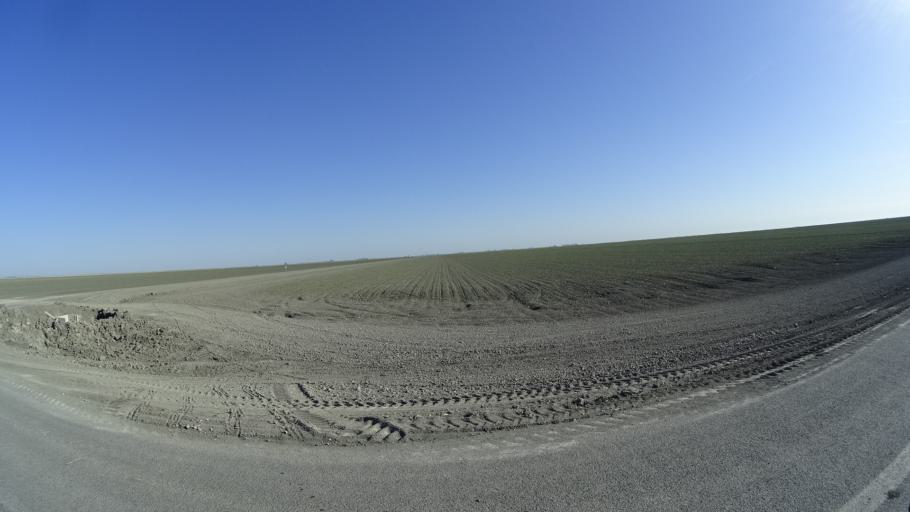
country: US
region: California
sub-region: Kings County
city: Stratford
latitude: 36.0795
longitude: -119.7976
